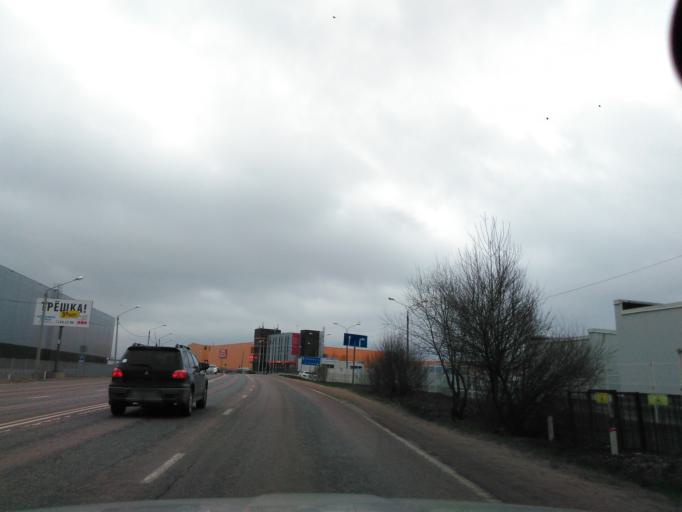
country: RU
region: Moskovskaya
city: Pavlovskaya Sloboda
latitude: 55.8144
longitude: 37.1137
